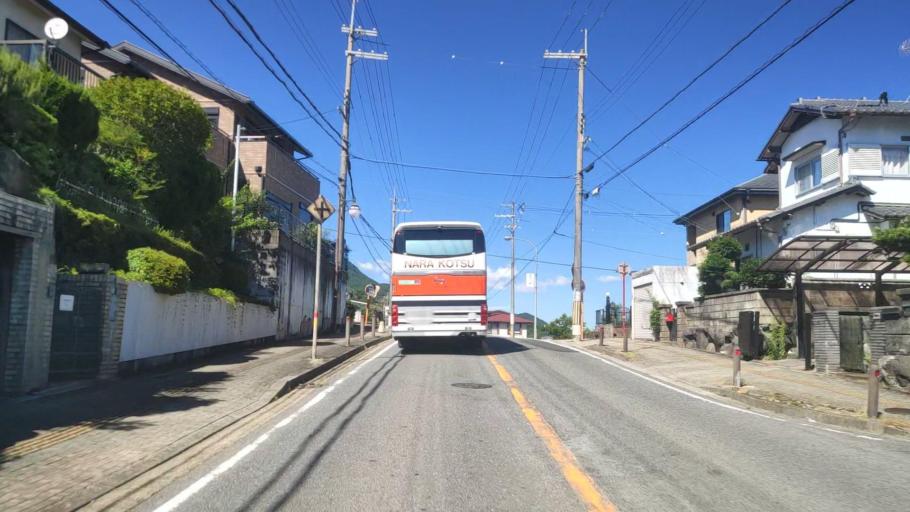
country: JP
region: Nara
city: Haibara-akanedai
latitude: 34.5357
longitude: 135.9499
